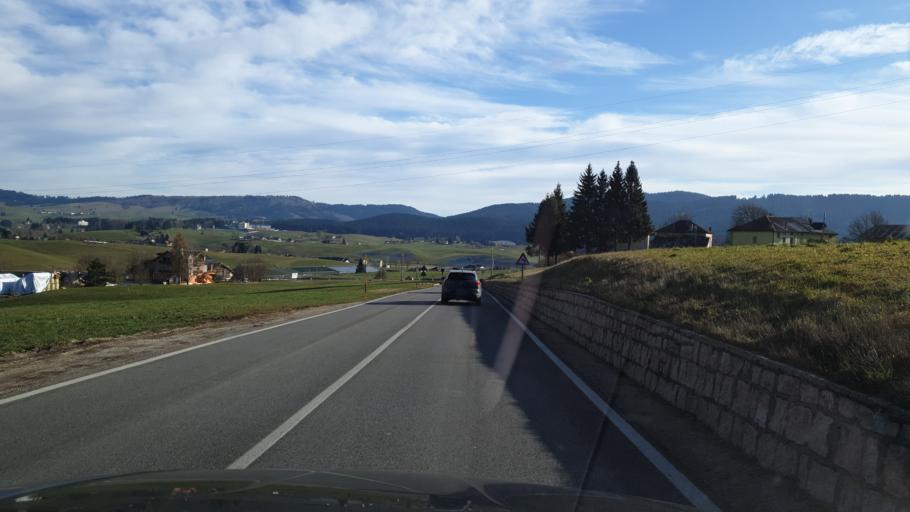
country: IT
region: Veneto
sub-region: Provincia di Vicenza
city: Canove di Roana
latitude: 45.8693
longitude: 11.4905
